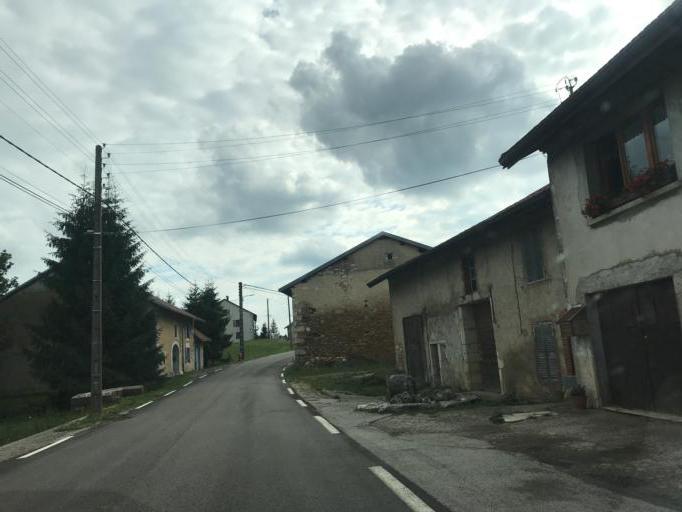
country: FR
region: Franche-Comte
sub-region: Departement du Jura
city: Valfin-les-Saint-Claude
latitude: 46.5055
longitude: 5.8652
